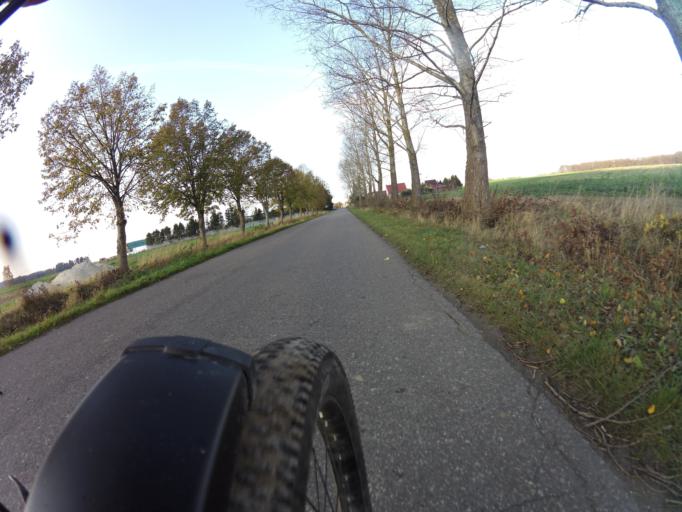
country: PL
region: Pomeranian Voivodeship
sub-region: Powiat pucki
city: Krokowa
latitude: 54.7562
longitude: 18.1844
